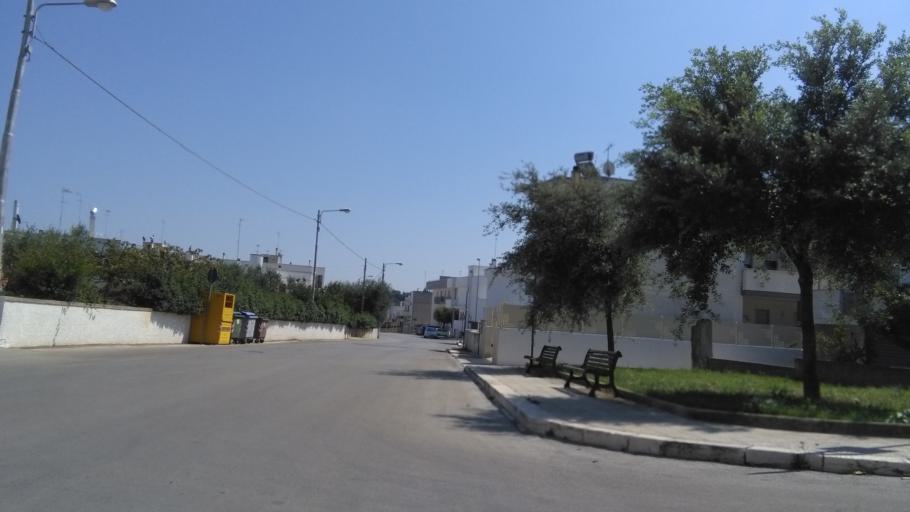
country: IT
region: Apulia
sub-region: Provincia di Bari
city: Alberobello
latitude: 40.7872
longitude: 17.2286
